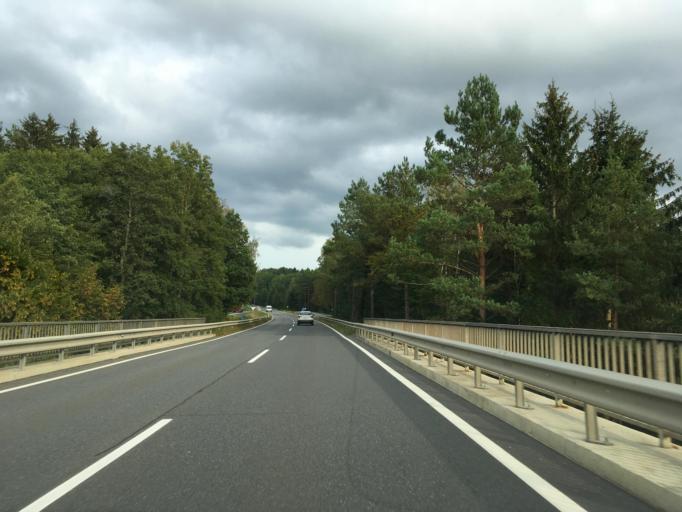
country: AT
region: Styria
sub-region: Politischer Bezirk Hartberg-Fuerstenfeld
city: Friedberg
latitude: 47.4169
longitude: 16.0385
